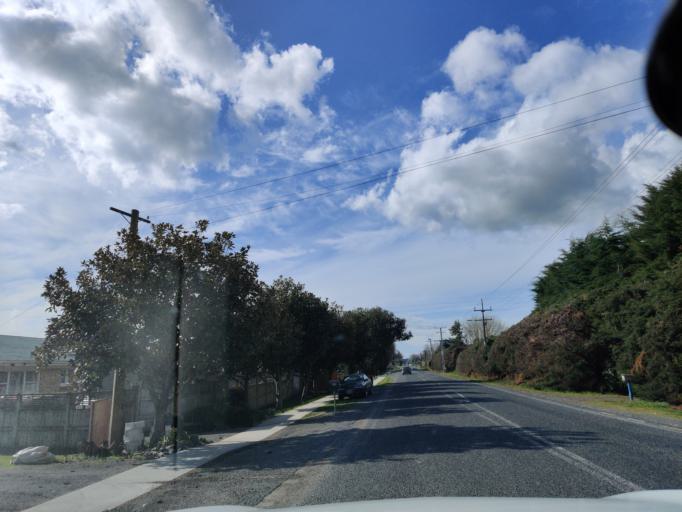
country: NZ
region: Waikato
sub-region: Waipa District
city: Cambridge
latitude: -37.8037
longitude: 175.3957
